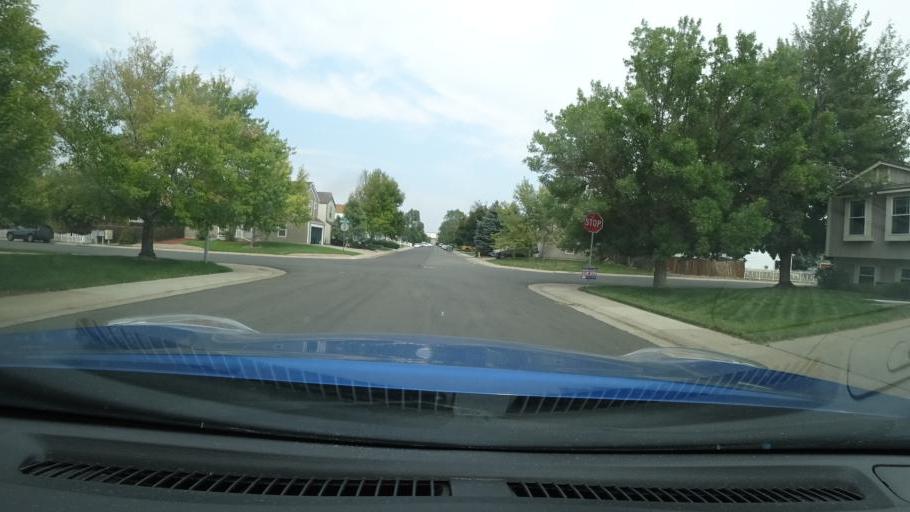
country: US
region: Colorado
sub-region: Adams County
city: Aurora
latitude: 39.7498
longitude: -104.7674
